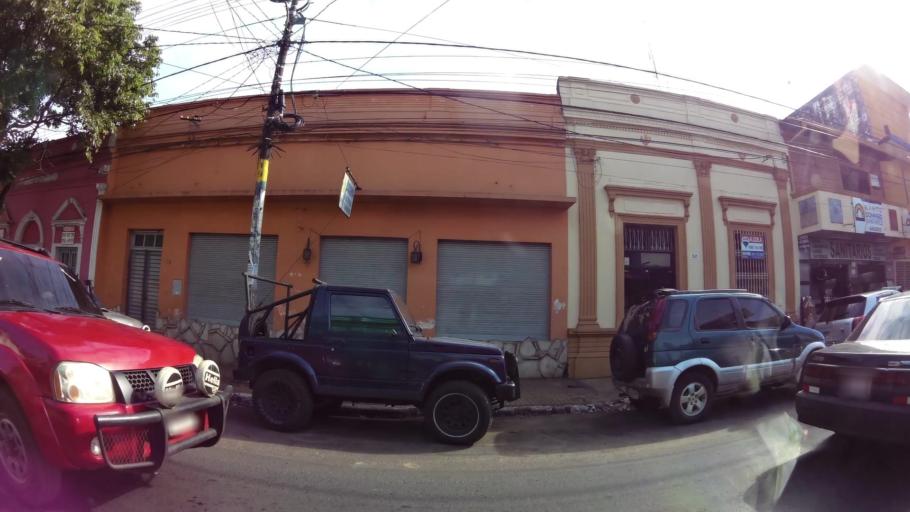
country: PY
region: Central
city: San Lorenzo
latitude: -25.2673
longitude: -57.4930
